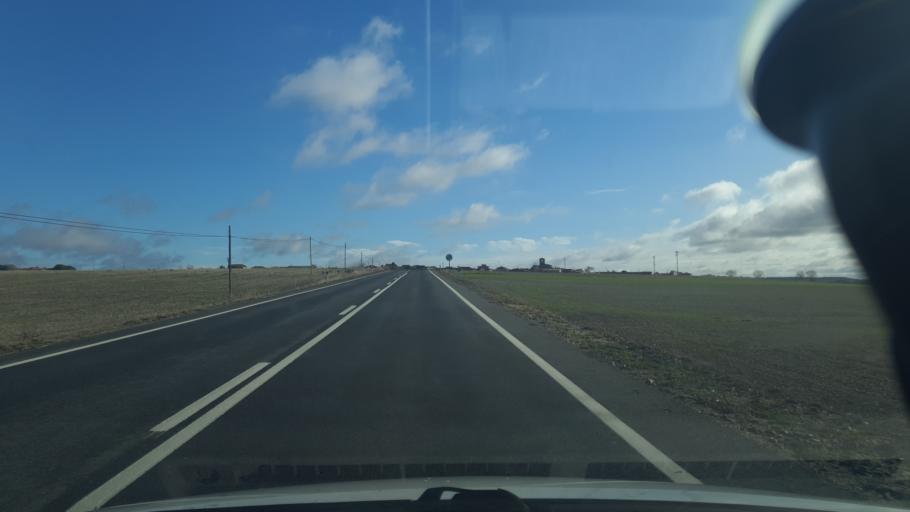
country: ES
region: Castille and Leon
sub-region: Provincia de Segovia
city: Codorniz
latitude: 41.0471
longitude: -4.6391
